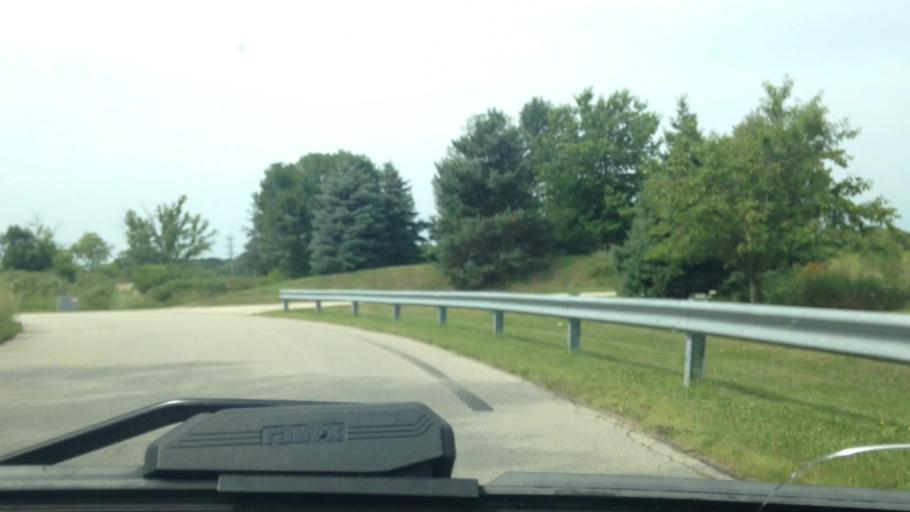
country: US
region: Wisconsin
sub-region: Waukesha County
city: Menomonee Falls
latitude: 43.1941
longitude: -88.1489
